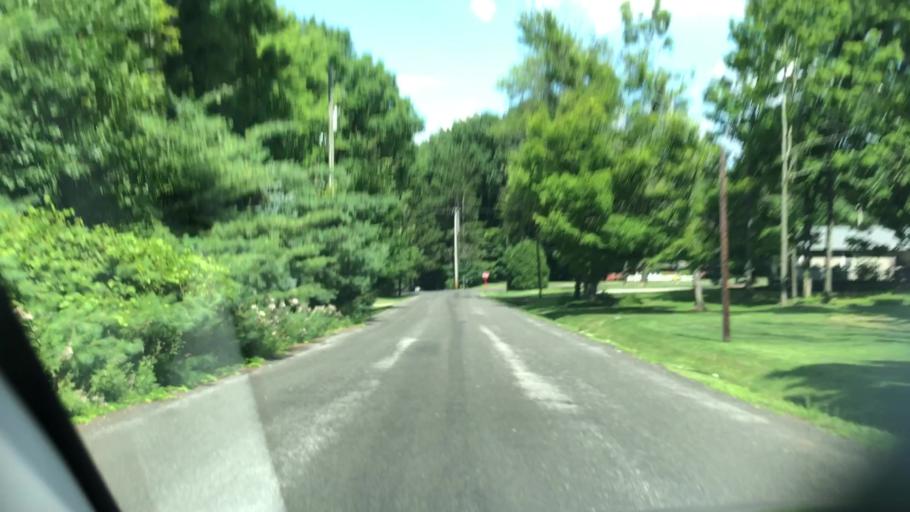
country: US
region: Ohio
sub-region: Summit County
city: Montrose-Ghent
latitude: 41.1579
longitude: -81.6493
